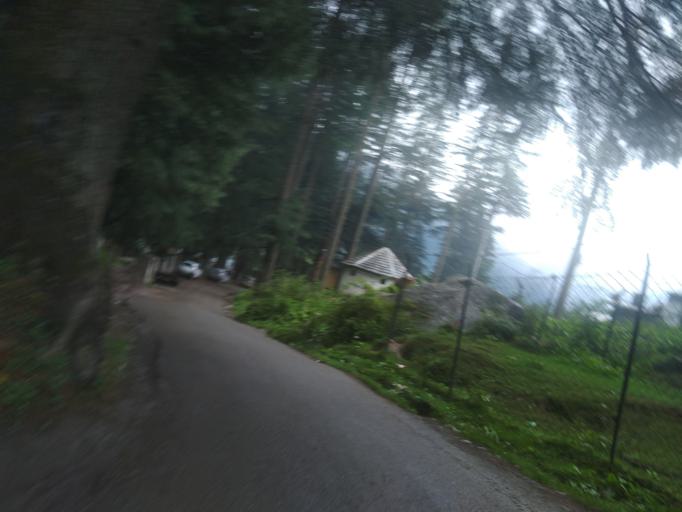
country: IN
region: Himachal Pradesh
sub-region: Kulu
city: Manali
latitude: 32.2471
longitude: 77.1793
